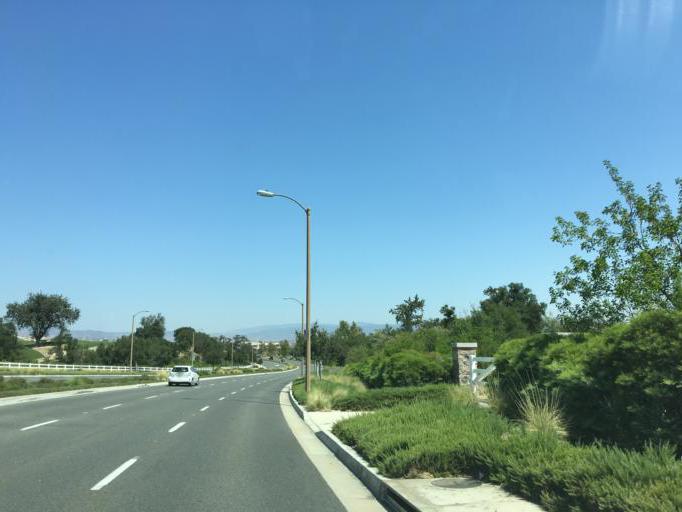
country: US
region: California
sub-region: Los Angeles County
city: Santa Clarita
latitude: 34.4003
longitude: -118.5759
